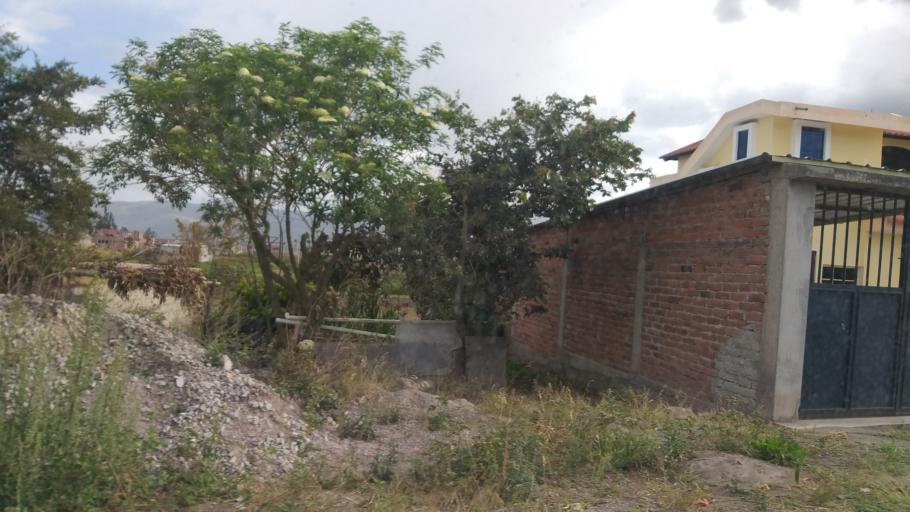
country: EC
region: Chimborazo
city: Riobamba
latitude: -1.6858
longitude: -78.6246
